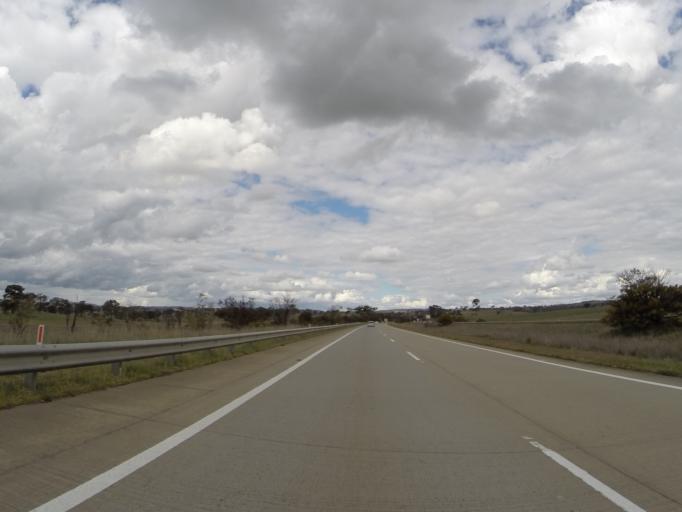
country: AU
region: New South Wales
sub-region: Yass Valley
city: Gundaroo
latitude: -34.8017
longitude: 149.2968
